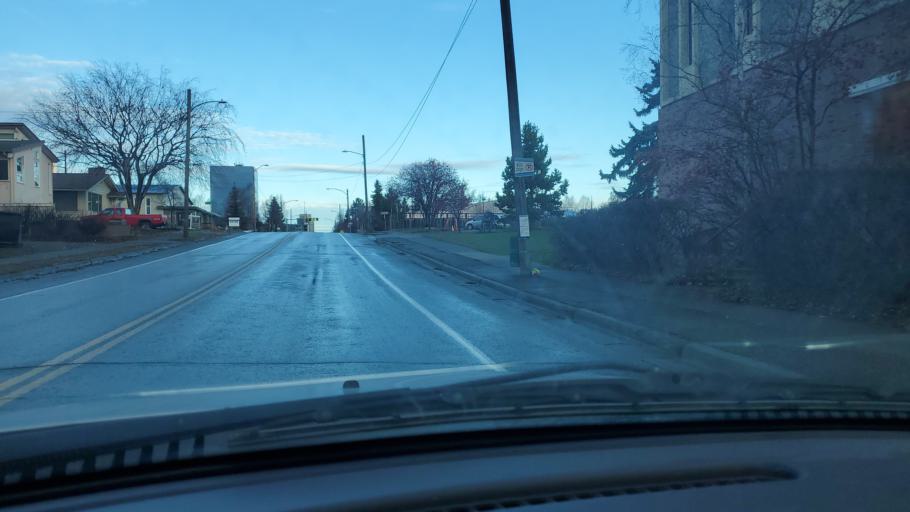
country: US
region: Alaska
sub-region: Anchorage Municipality
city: Anchorage
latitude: 61.2089
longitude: -149.8914
